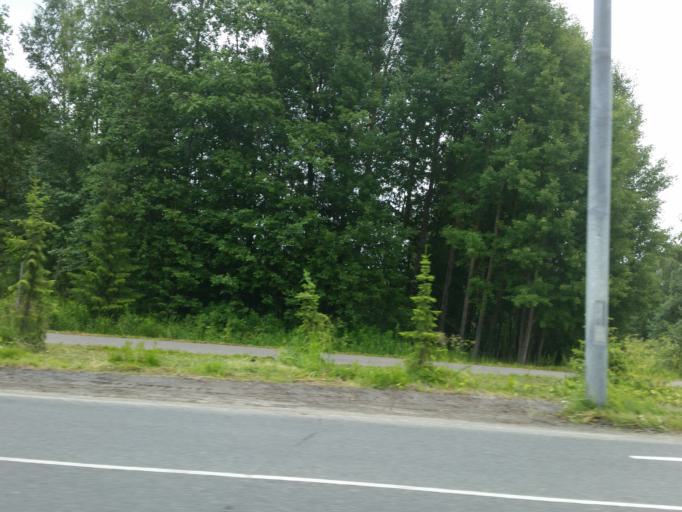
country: FI
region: Northern Savo
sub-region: Kuopio
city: Kuopio
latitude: 62.8835
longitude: 27.6431
